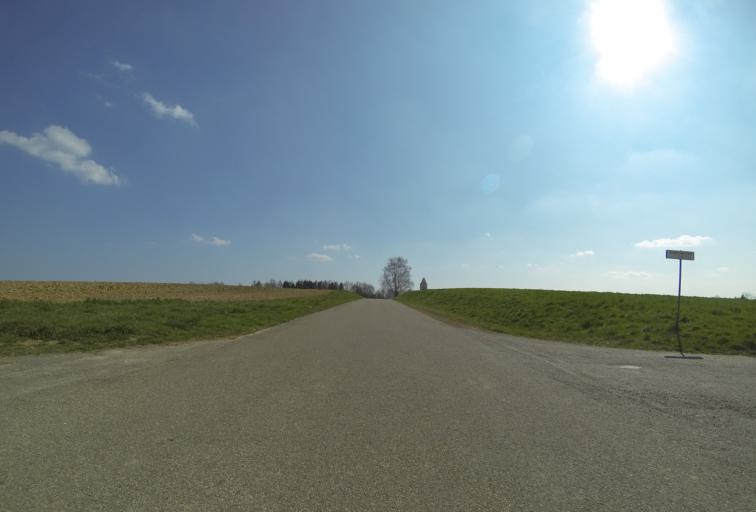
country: DE
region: Baden-Wuerttemberg
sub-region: Tuebingen Region
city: Huttisheim
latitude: 48.2815
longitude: 9.9497
